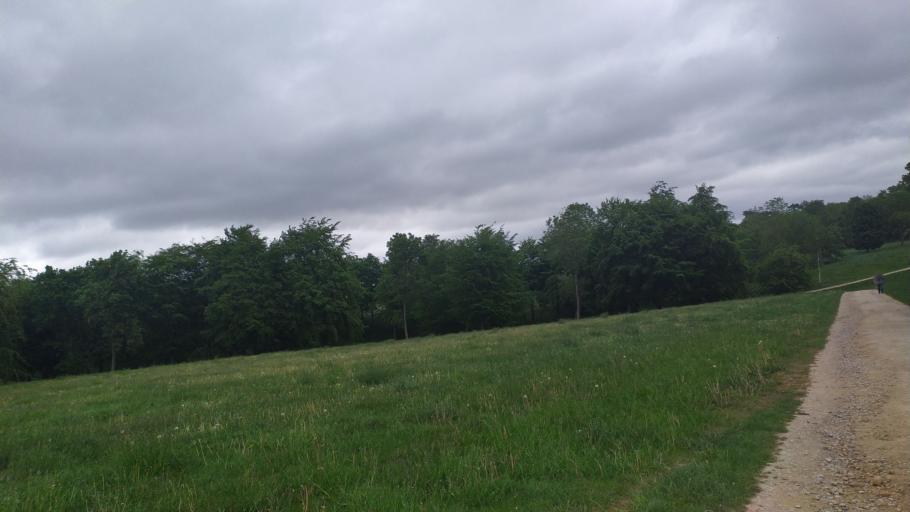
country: GB
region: England
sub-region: City and Borough of Leeds
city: Bramham
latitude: 53.8605
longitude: -1.3819
